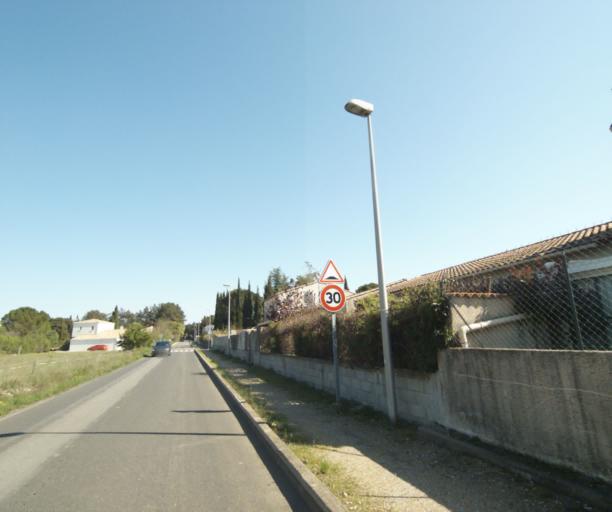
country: FR
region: Languedoc-Roussillon
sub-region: Departement de l'Herault
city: Castries
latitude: 43.6856
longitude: 3.9786
